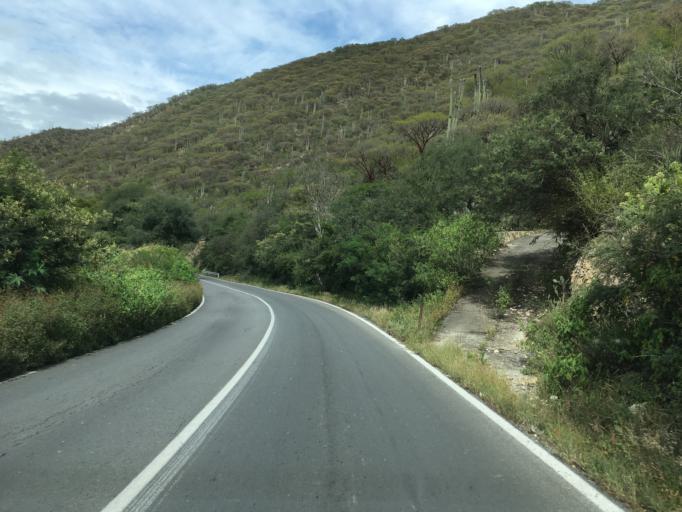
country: MX
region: Hidalgo
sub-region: San Agustin Metzquititlan
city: Mezquititlan
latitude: 20.5199
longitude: -98.7158
